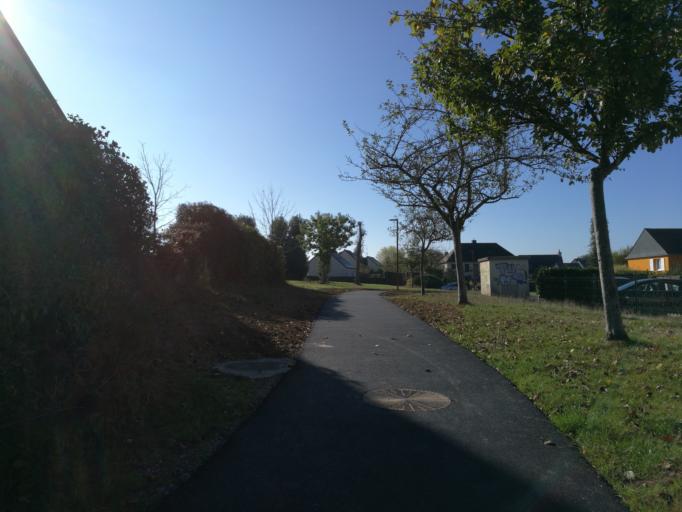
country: FR
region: Brittany
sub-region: Departement d'Ille-et-Vilaine
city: Bedee
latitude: 48.1775
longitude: -1.9394
